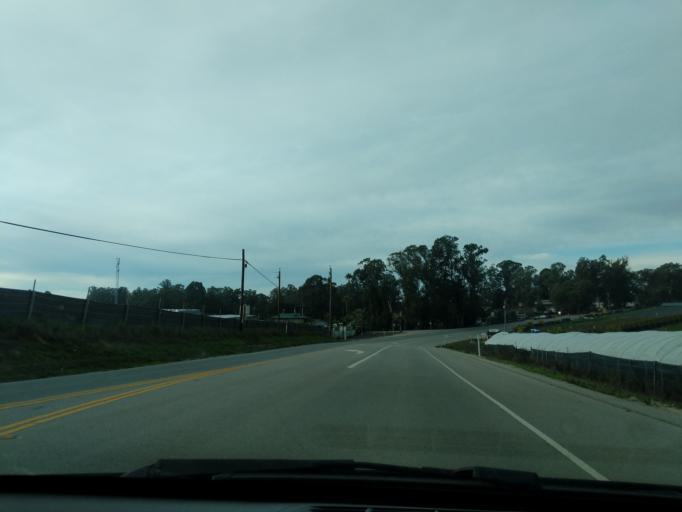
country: US
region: California
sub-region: San Luis Obispo County
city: Callender
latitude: 35.0389
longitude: -120.5665
